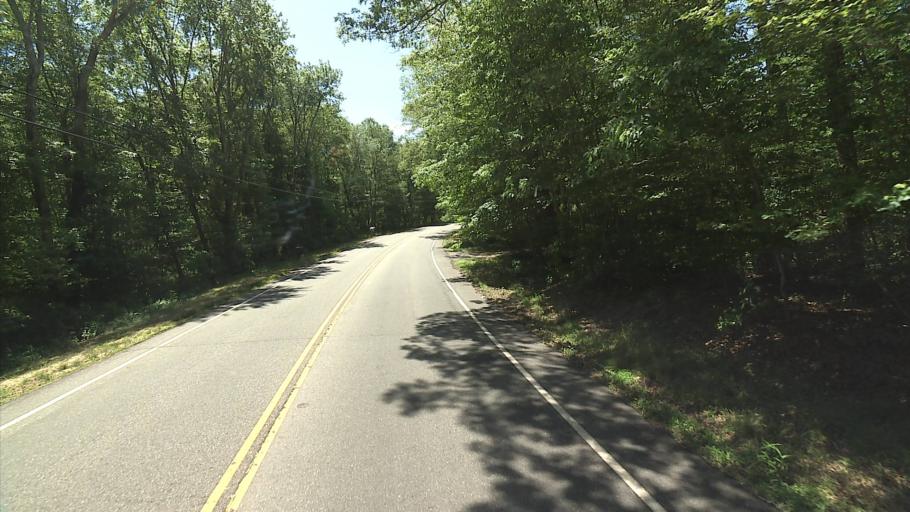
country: US
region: Rhode Island
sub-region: Washington County
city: Hopkinton
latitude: 41.4983
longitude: -71.8316
